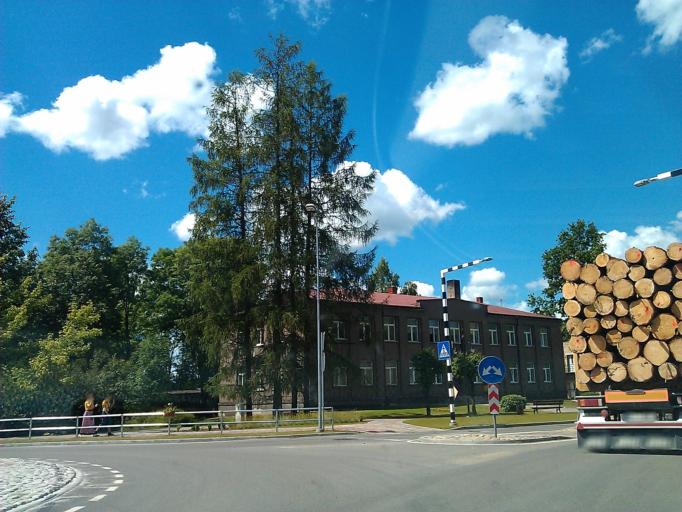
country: LV
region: Vilanu
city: Vilani
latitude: 56.5503
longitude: 26.9228
